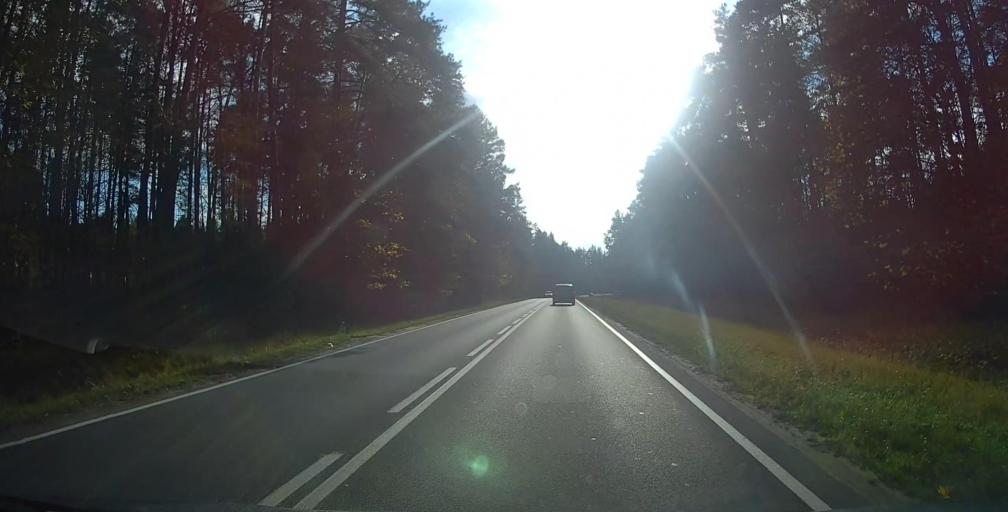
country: PL
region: Warmian-Masurian Voivodeship
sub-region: Powiat elcki
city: Elk
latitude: 53.7783
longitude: 22.3456
